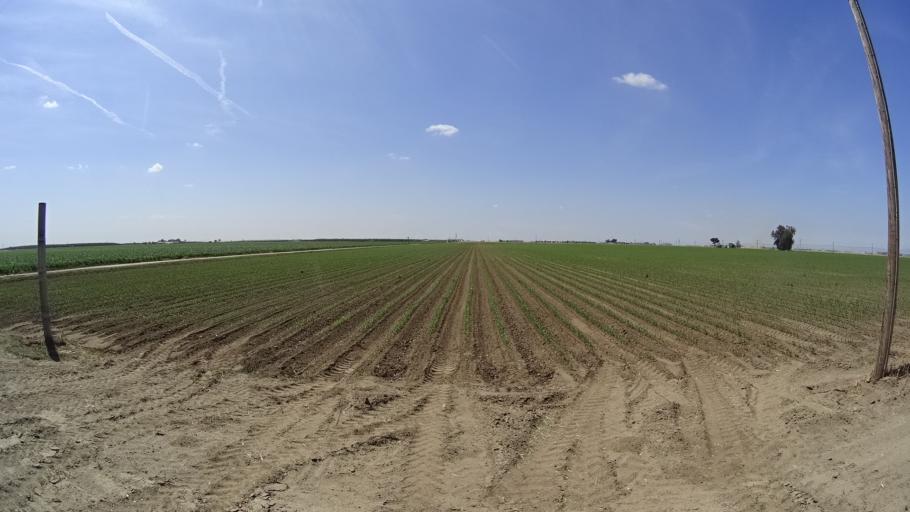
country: US
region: California
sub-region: Kings County
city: Home Garden
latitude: 36.2694
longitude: -119.6150
